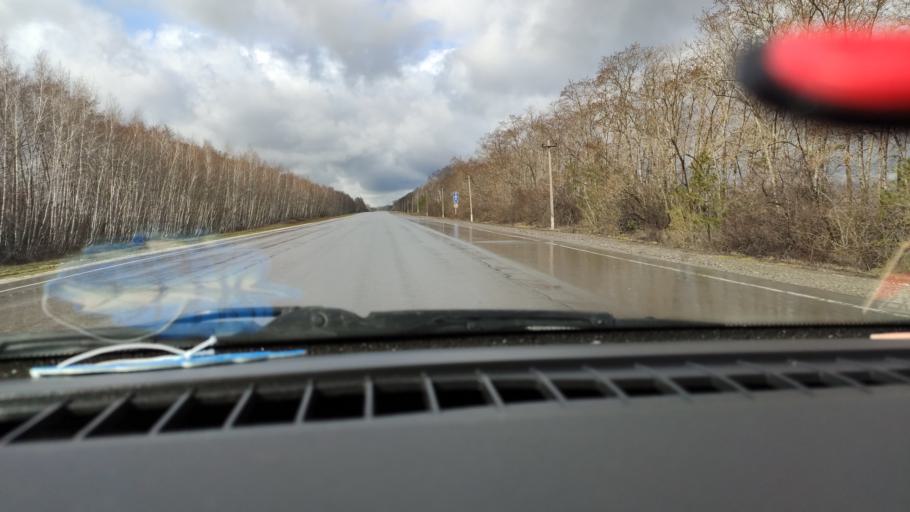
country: RU
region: Samara
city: Yelkhovka
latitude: 54.0596
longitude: 50.3077
